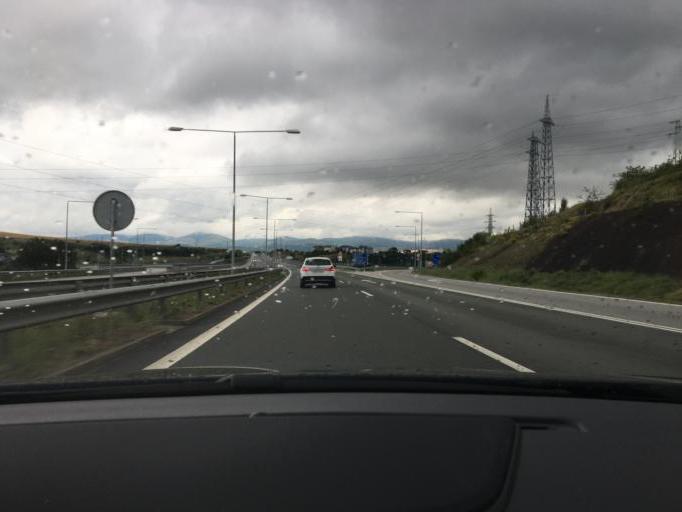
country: BG
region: Pernik
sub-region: Obshtina Pernik
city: Pernik
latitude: 42.6047
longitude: 23.1268
